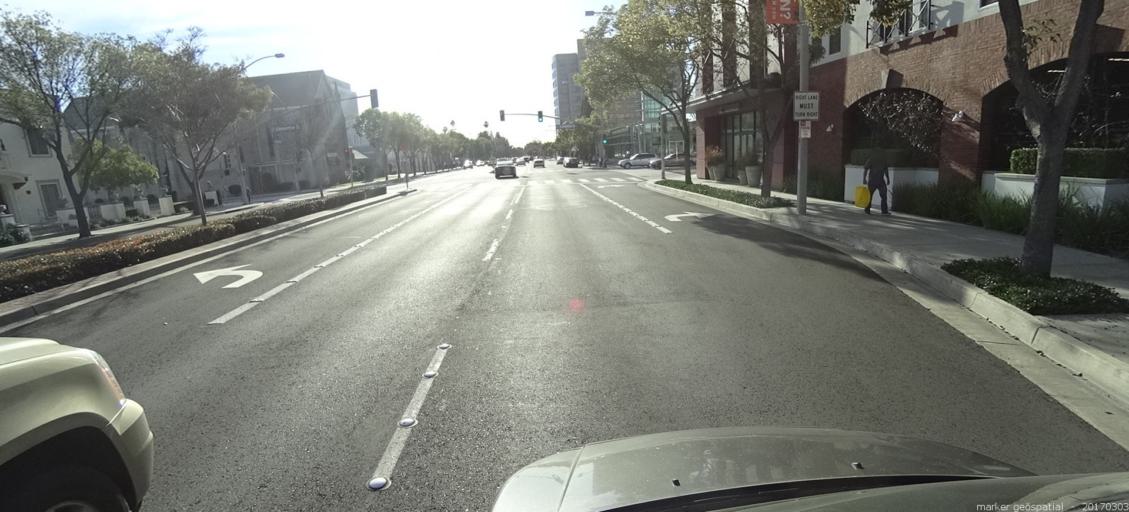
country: US
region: California
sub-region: Orange County
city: Anaheim
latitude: 33.8329
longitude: -117.9157
